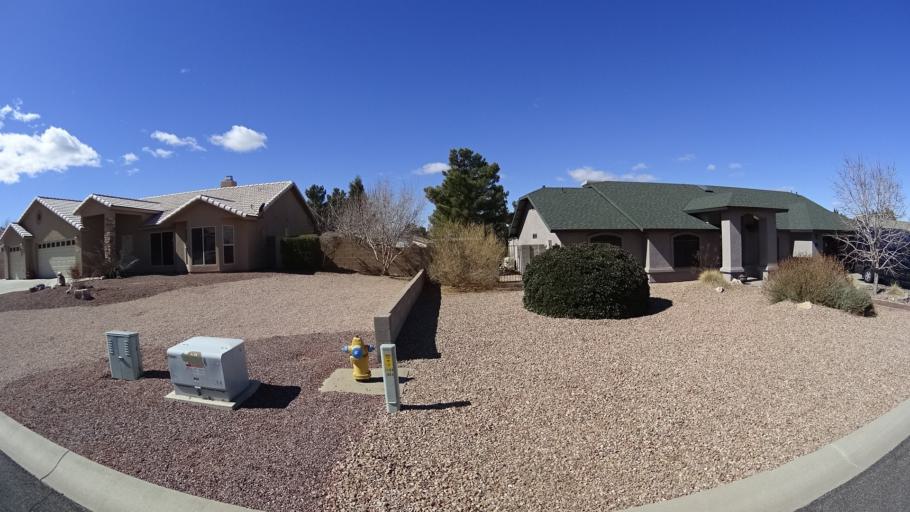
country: US
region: Arizona
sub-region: Mohave County
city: Kingman
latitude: 35.2003
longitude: -113.9706
